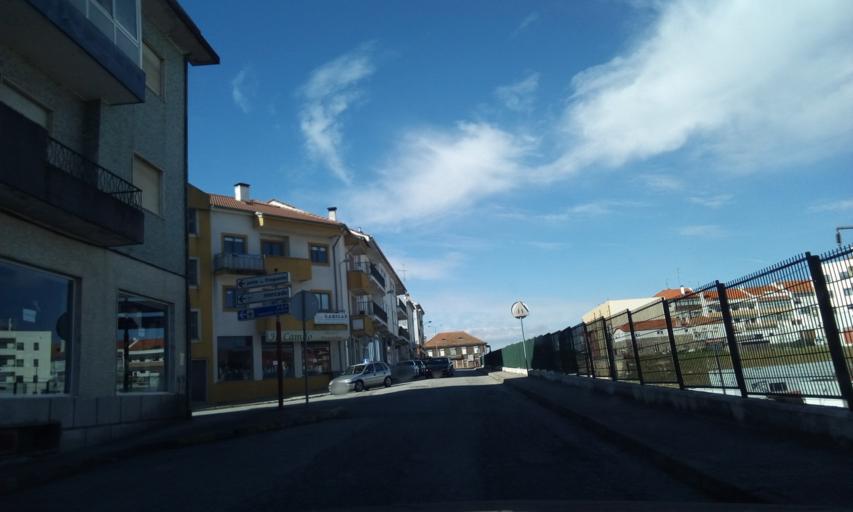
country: PT
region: Guarda
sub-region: Guarda
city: Sequeira
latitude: 40.5543
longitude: -7.2410
